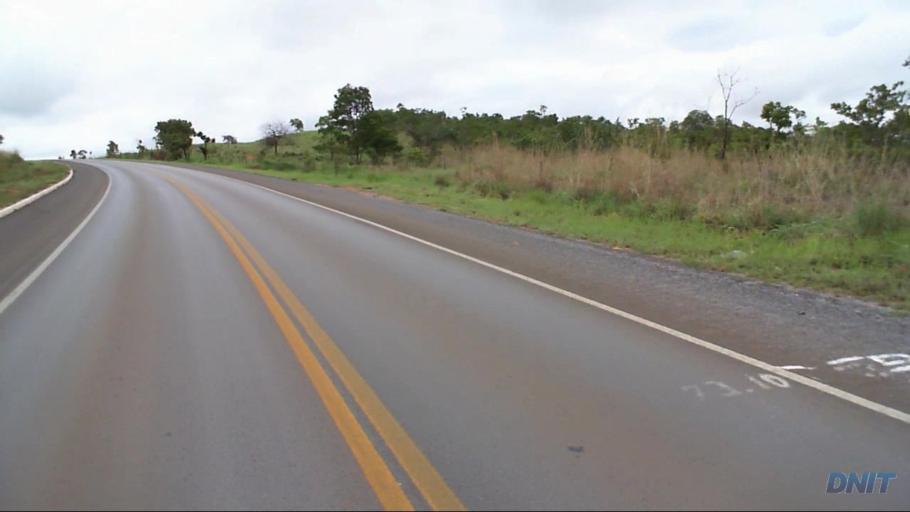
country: BR
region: Goias
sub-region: Padre Bernardo
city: Padre Bernardo
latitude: -15.2163
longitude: -48.5118
